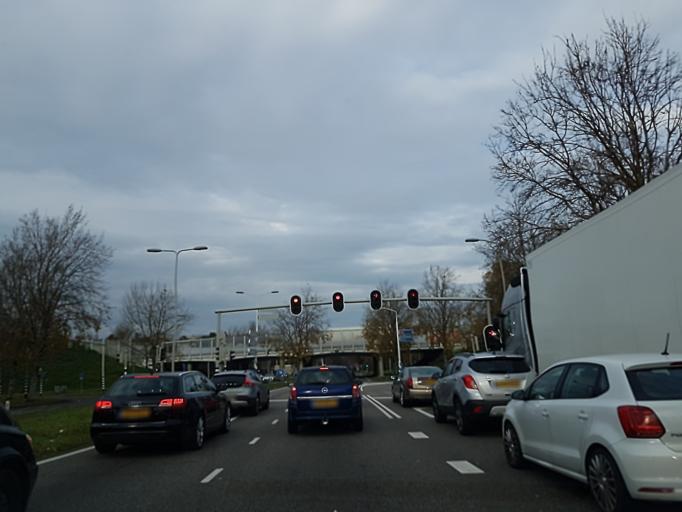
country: NL
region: North Brabant
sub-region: Roosendaal
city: Roosendaal
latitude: 51.5242
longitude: 4.4656
